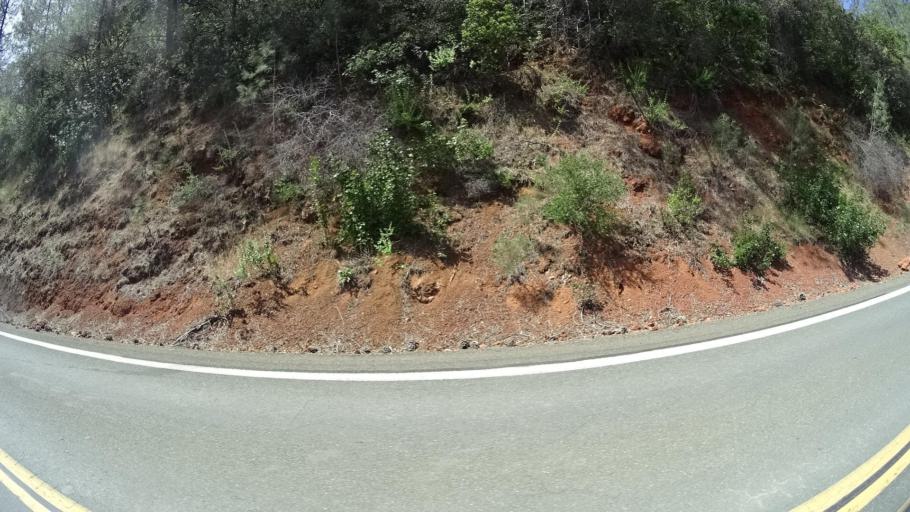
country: US
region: California
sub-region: Lake County
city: Lower Lake
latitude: 38.9165
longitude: -122.6594
